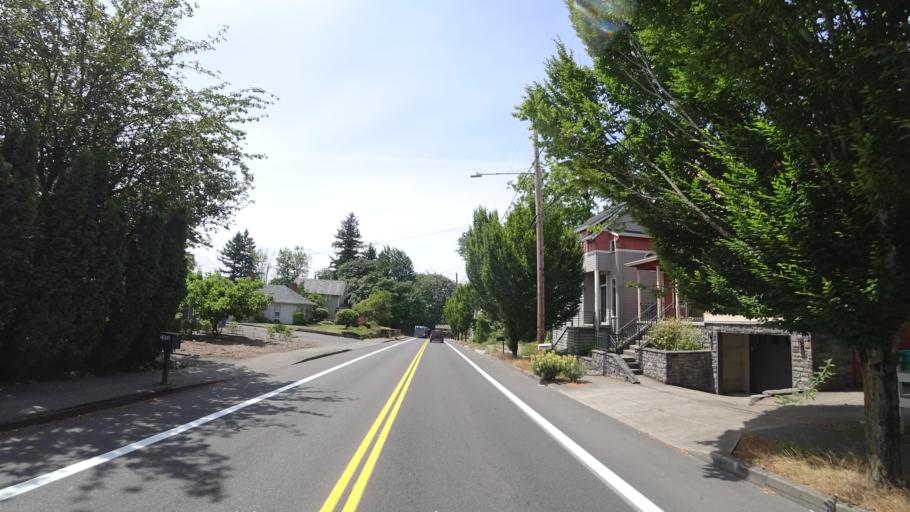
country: US
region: Oregon
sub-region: Clackamas County
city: Milwaukie
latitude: 45.4633
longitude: -122.6317
